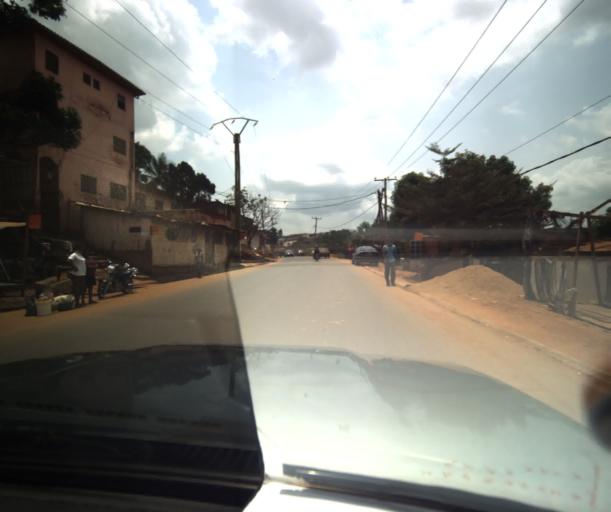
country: CM
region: Centre
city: Yaounde
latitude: 3.8473
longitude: 11.4804
